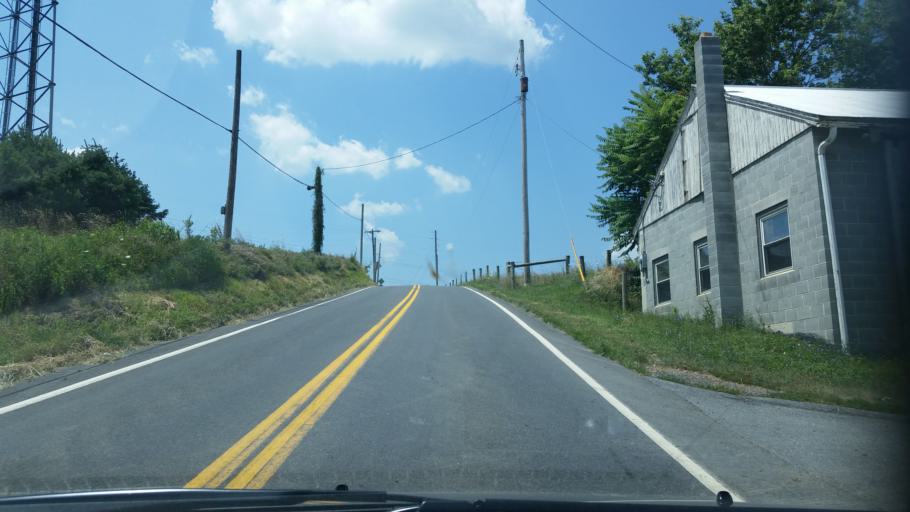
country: US
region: Pennsylvania
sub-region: Dauphin County
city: Hummelstown
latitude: 40.2875
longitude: -76.7330
